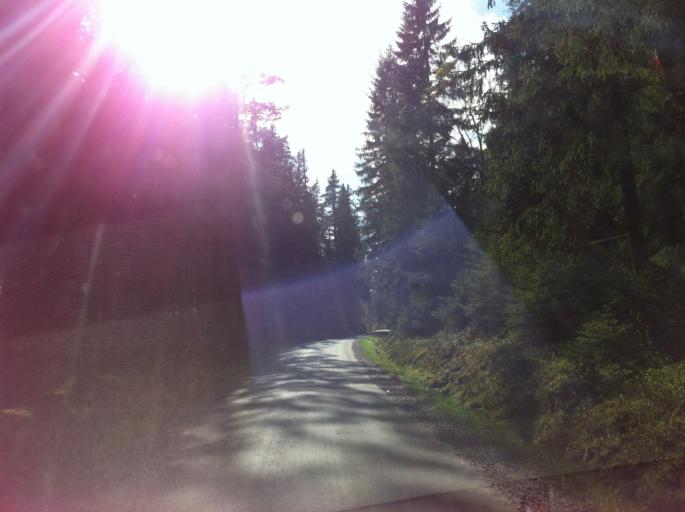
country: SE
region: Vaestra Goetaland
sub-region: Bollebygds Kommun
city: Bollebygd
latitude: 57.7732
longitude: 12.5971
